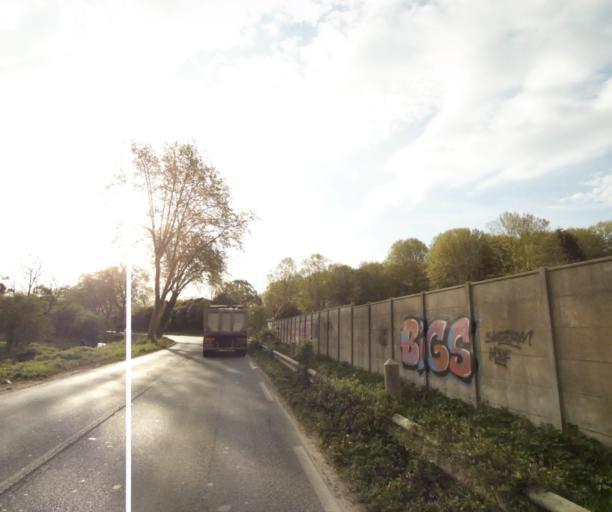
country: FR
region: Ile-de-France
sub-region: Departement de Seine-et-Marne
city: Torcy
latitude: 48.8591
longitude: 2.6514
